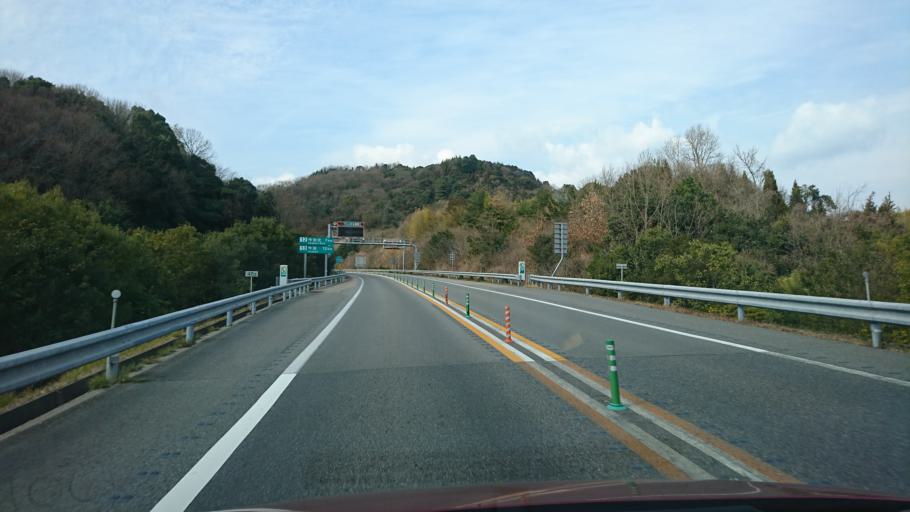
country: JP
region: Hiroshima
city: Innoshima
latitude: 34.1307
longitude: 133.0299
